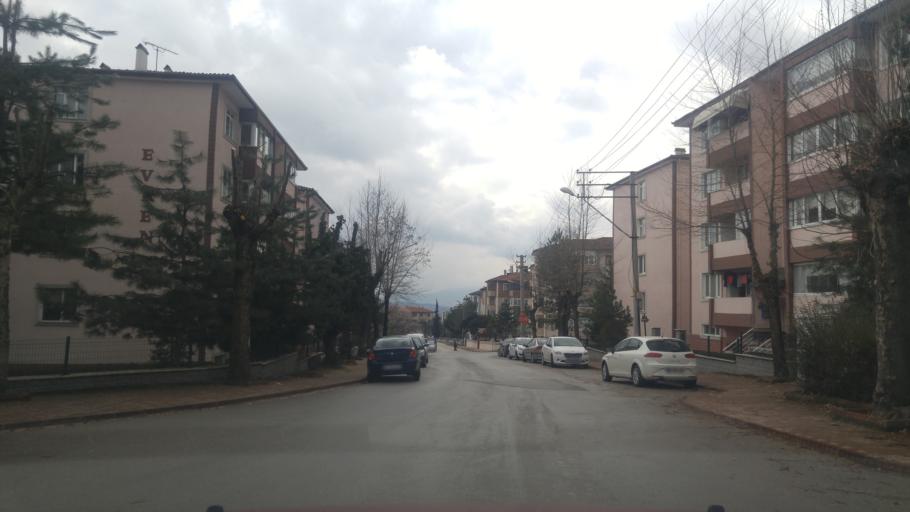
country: TR
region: Karabuk
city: Safranbolu
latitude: 41.2510
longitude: 32.6761
